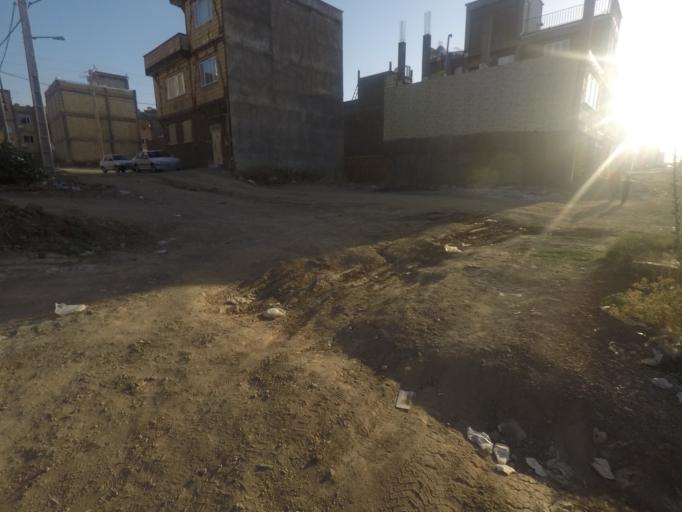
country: IR
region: Kordestan
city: Marivan
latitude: 35.5093
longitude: 46.1907
